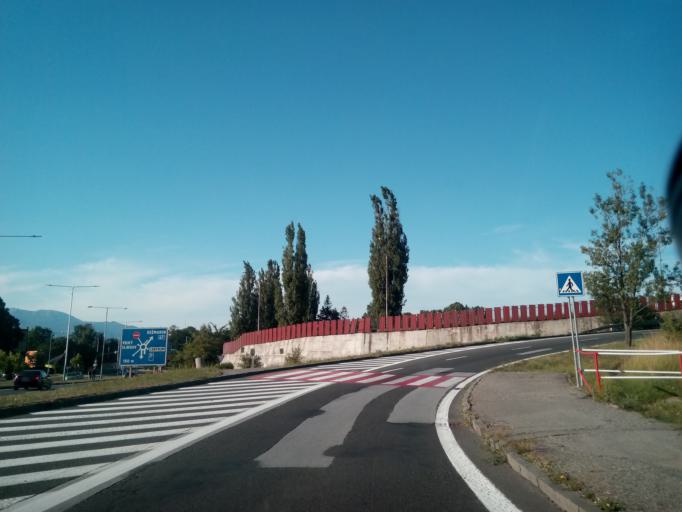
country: SK
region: Presovsky
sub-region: Okres Poprad
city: Poprad
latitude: 49.0519
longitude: 20.2936
